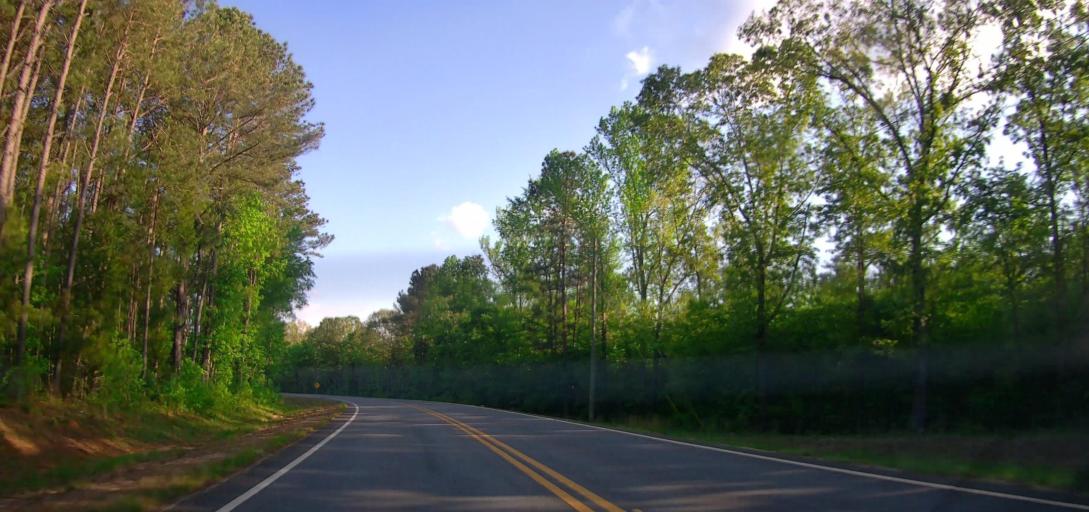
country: US
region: Georgia
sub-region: Putnam County
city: Eatonton
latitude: 33.3213
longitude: -83.4980
